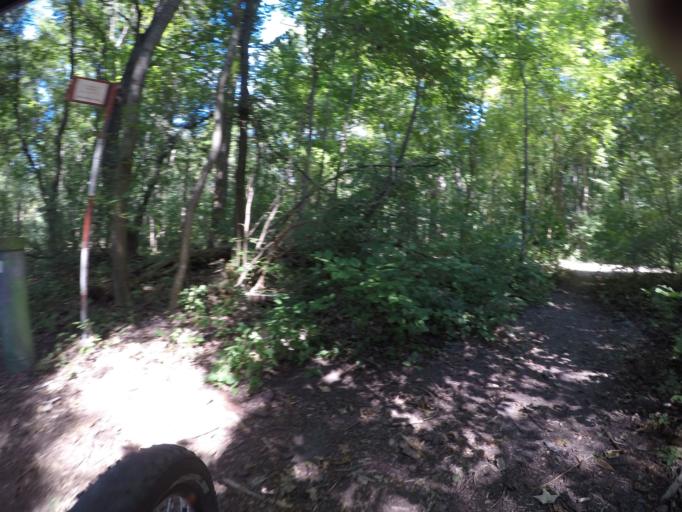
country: AT
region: Lower Austria
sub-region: Politischer Bezirk Wien-Umgebung
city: Schwechat
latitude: 48.1869
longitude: 16.4896
